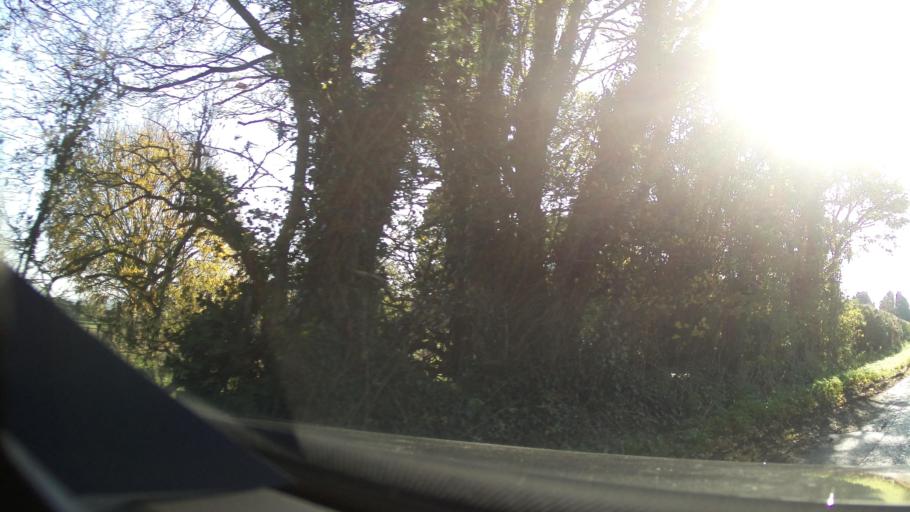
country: GB
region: England
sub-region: Somerset
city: Milborne Port
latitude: 51.0149
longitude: -2.5058
